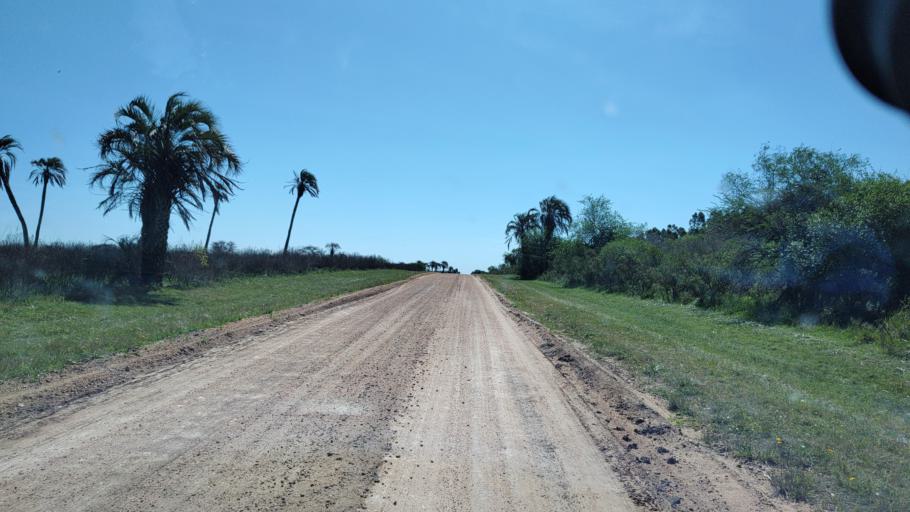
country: AR
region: Entre Rios
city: Ubajay
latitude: -31.8577
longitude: -58.2816
